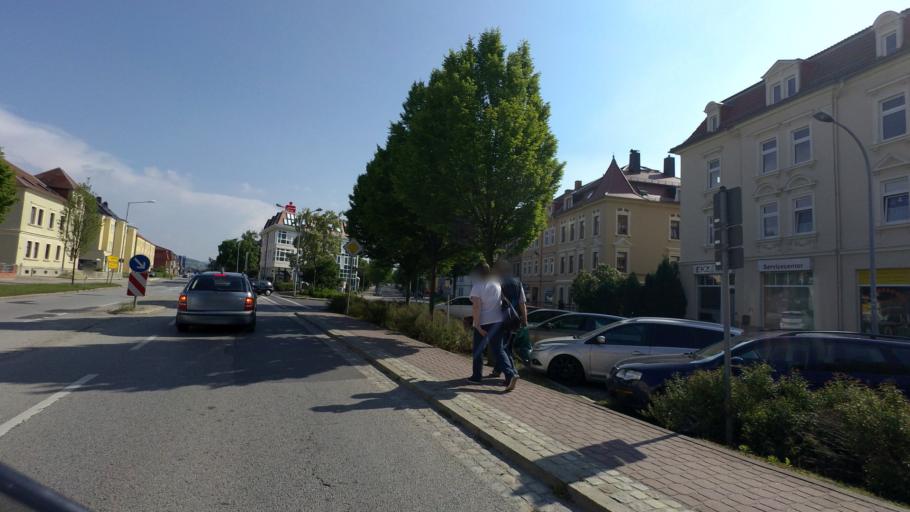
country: DE
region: Saxony
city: Bautzen
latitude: 51.1724
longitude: 14.4238
